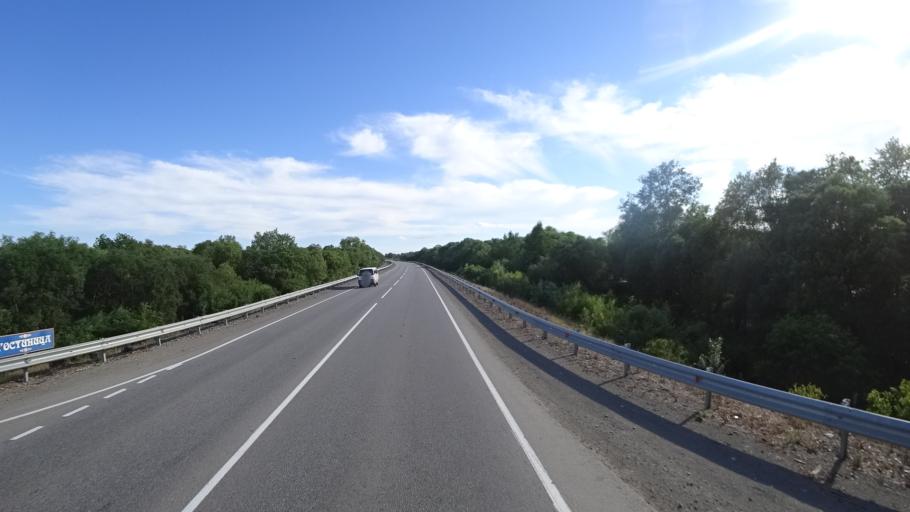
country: RU
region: Khabarovsk Krai
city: Khor
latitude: 47.8829
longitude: 134.9720
